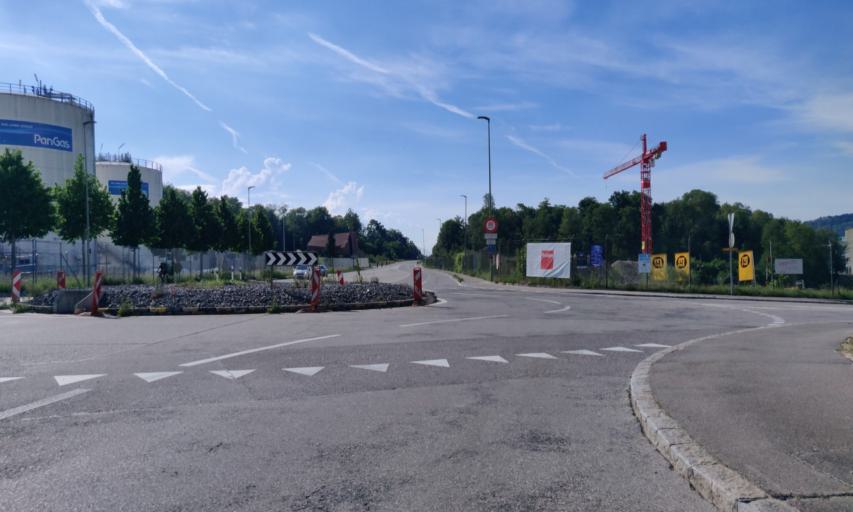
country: CH
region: Basel-Landschaft
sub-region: Bezirk Arlesheim
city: Muttenz
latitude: 47.5370
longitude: 7.6610
